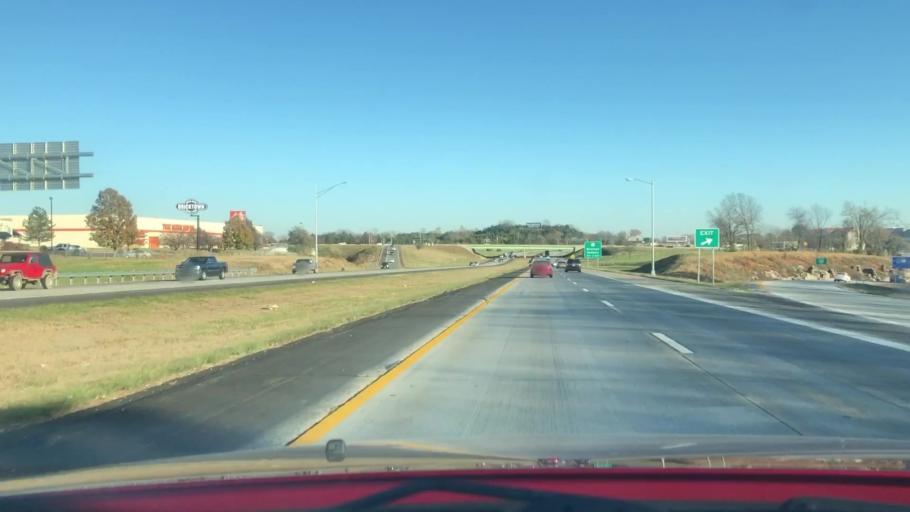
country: US
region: Missouri
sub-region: Greene County
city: Springfield
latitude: 37.1402
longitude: -93.2589
